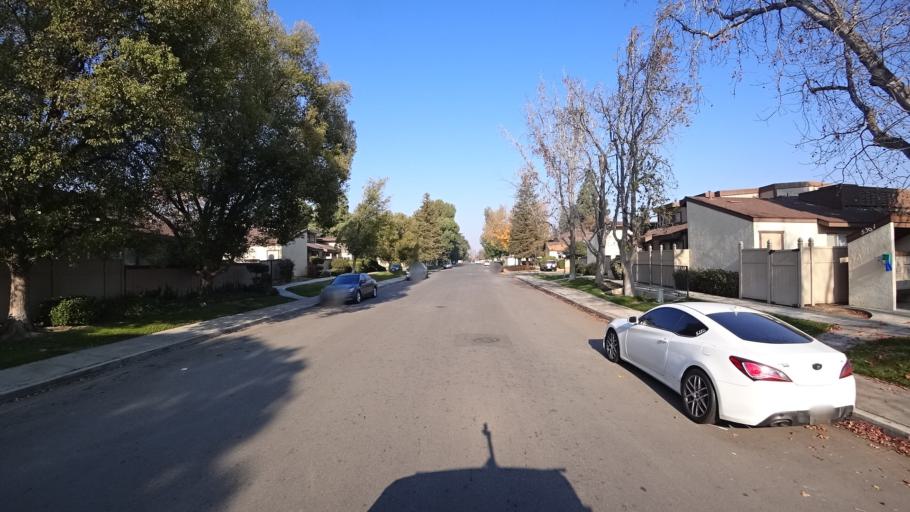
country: US
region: California
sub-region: Kern County
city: Bakersfield
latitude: 35.3575
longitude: -119.0585
